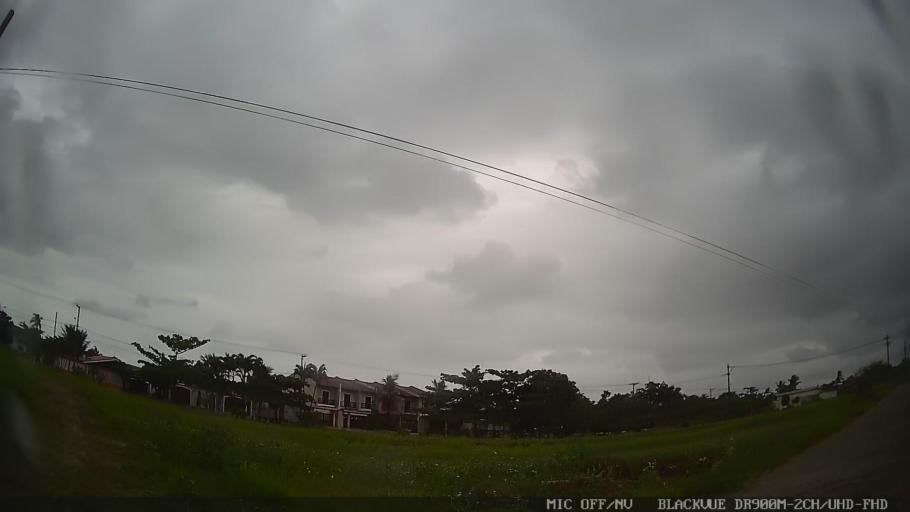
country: BR
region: Sao Paulo
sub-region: Itanhaem
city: Itanhaem
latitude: -24.1398
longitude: -46.7087
